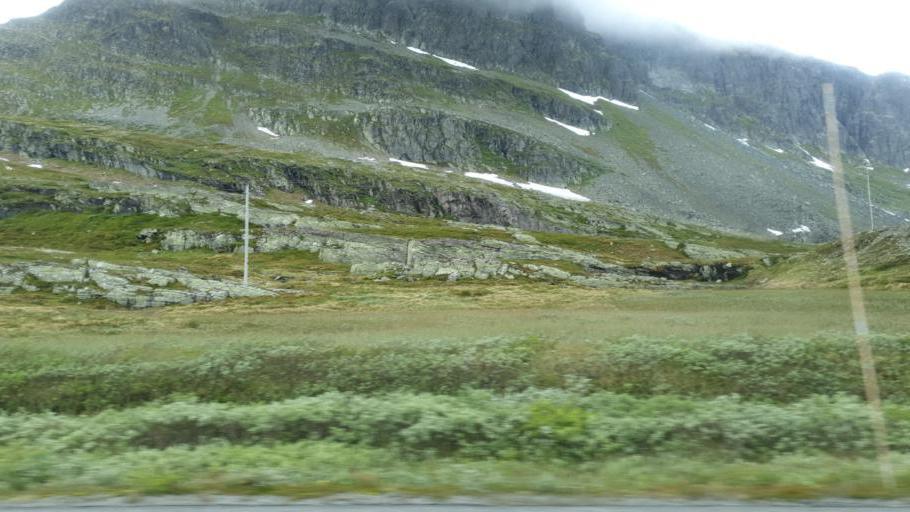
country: NO
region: Oppland
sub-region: Vestre Slidre
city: Slidre
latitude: 61.2948
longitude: 8.8139
